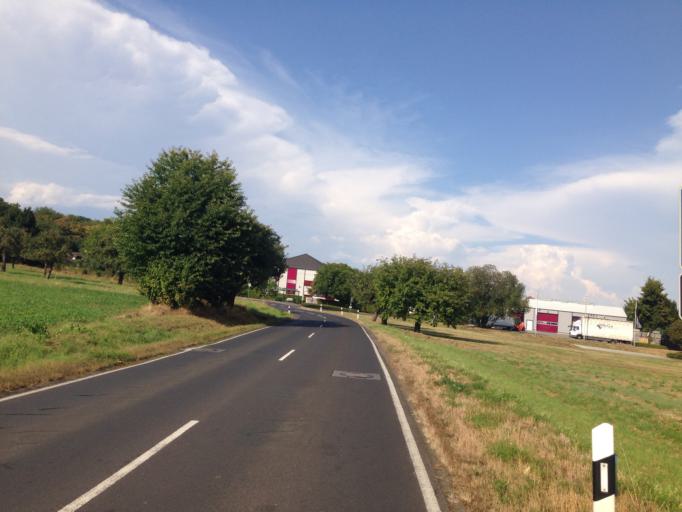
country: DE
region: Hesse
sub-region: Regierungsbezirk Giessen
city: Giessen
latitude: 50.6169
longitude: 8.6609
